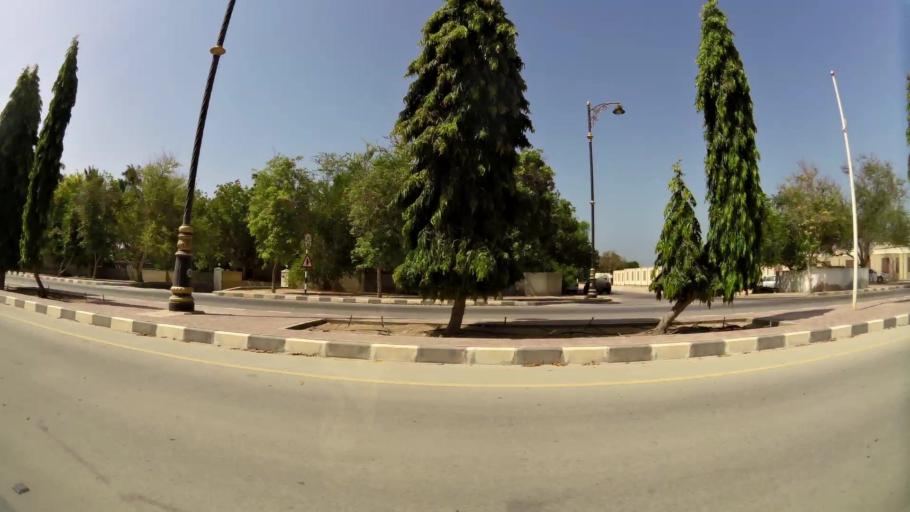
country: OM
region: Zufar
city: Salalah
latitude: 17.0262
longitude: 54.1530
